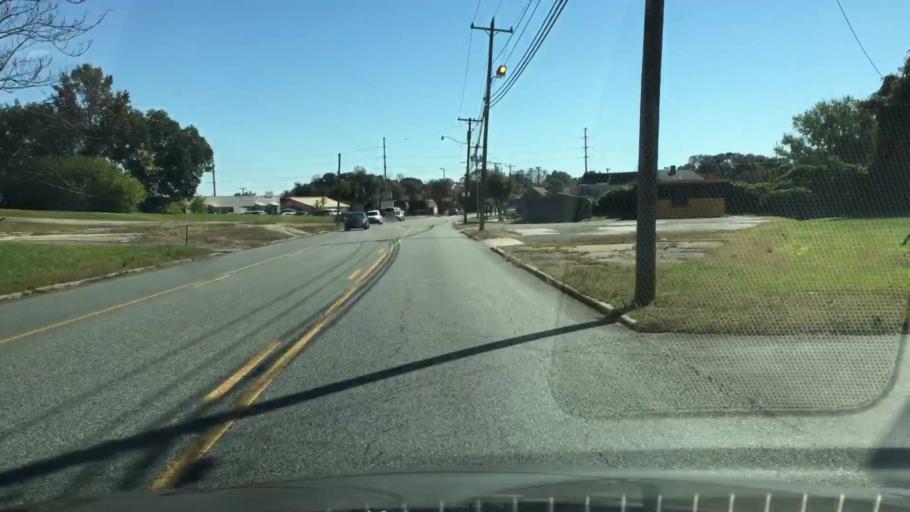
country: US
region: North Carolina
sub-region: Rockingham County
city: Reidsville
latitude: 36.3440
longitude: -79.6642
